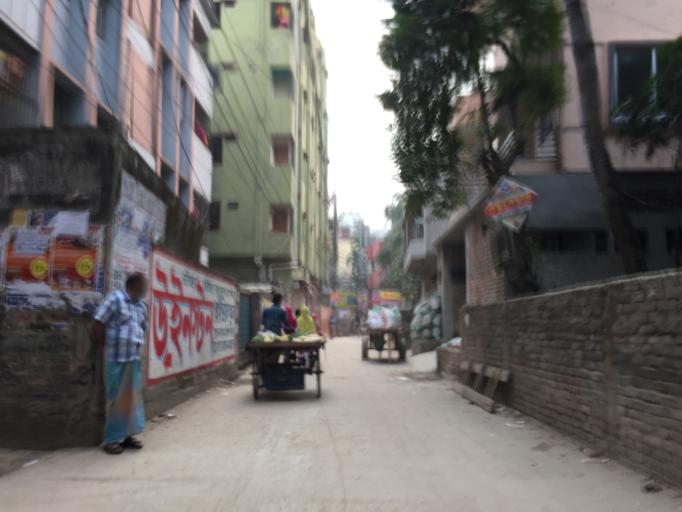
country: BD
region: Dhaka
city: Azimpur
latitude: 23.7952
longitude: 90.3617
